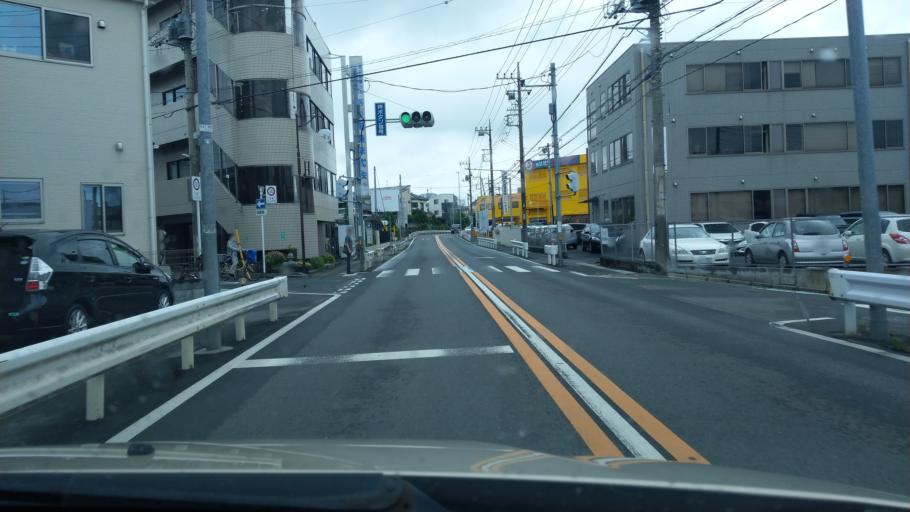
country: JP
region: Saitama
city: Yono
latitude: 35.9022
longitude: 139.6369
